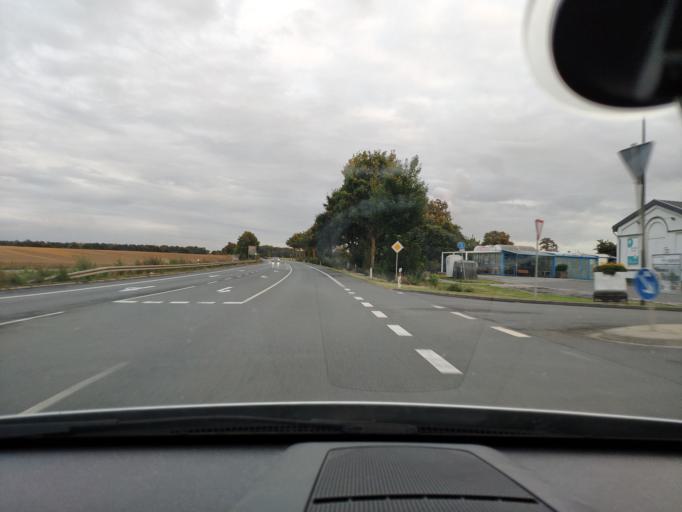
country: DE
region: North Rhine-Westphalia
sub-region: Regierungsbezirk Koln
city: Aldenhoven
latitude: 50.9059
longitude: 6.2623
